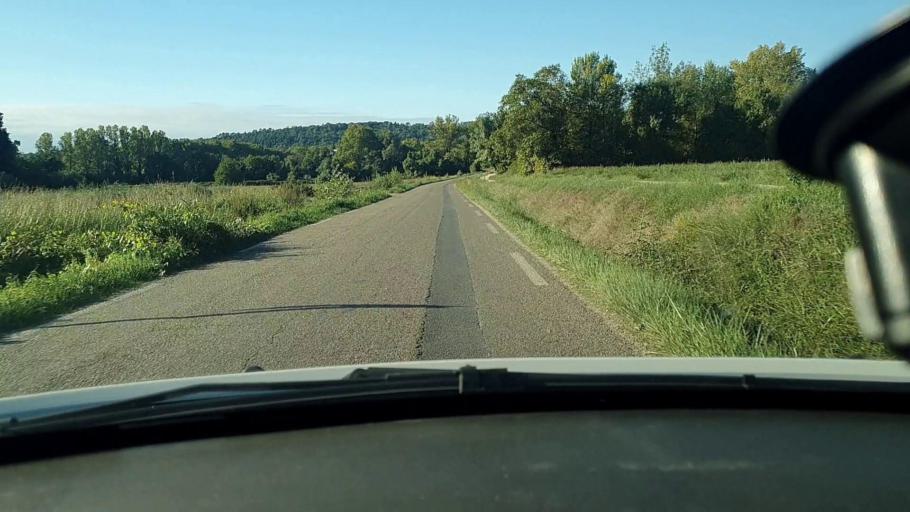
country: FR
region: Languedoc-Roussillon
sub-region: Departement du Gard
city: Goudargues
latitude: 44.2096
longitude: 4.4676
